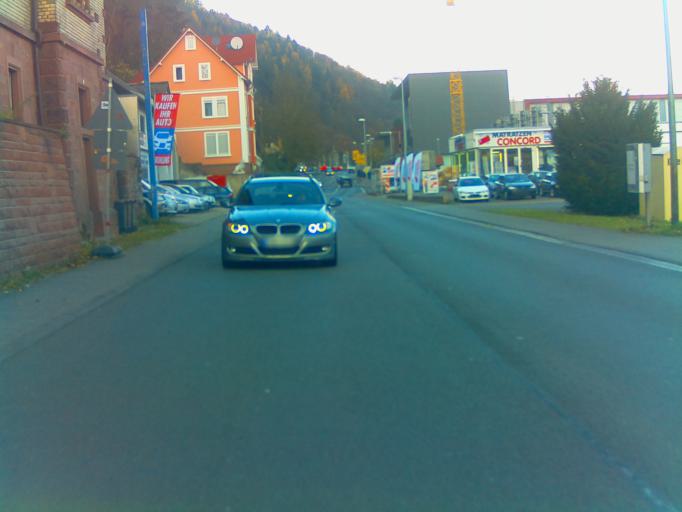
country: DE
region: Baden-Wuerttemberg
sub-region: Regierungsbezirk Stuttgart
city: Wertheim
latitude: 49.7650
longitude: 9.5093
